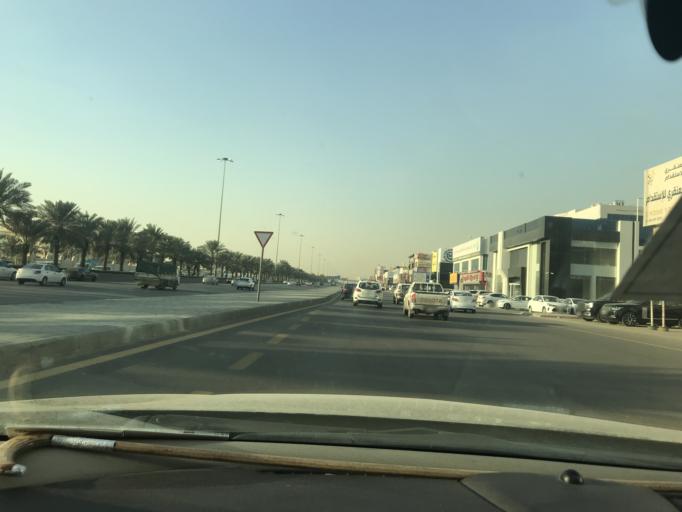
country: SA
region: Ar Riyad
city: Riyadh
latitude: 24.7456
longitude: 46.7464
